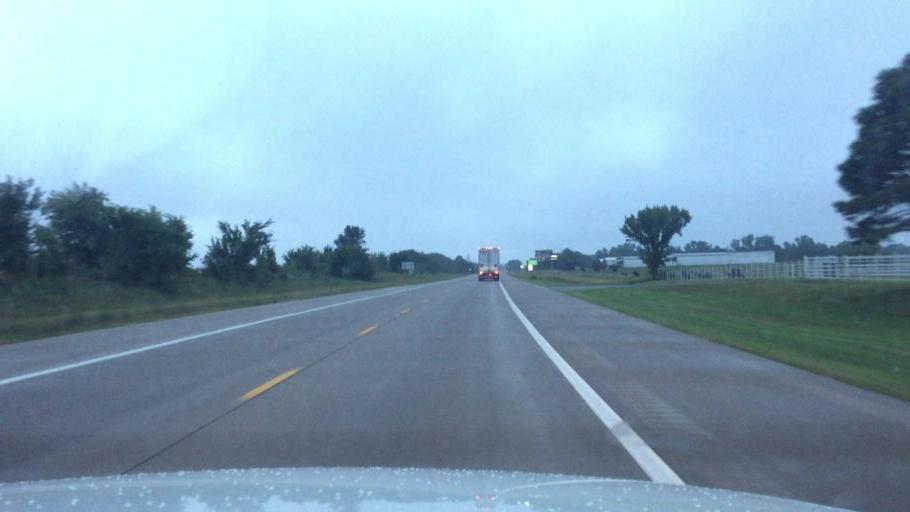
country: US
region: Kansas
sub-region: Neosho County
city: Chanute
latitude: 37.5012
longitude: -95.4706
